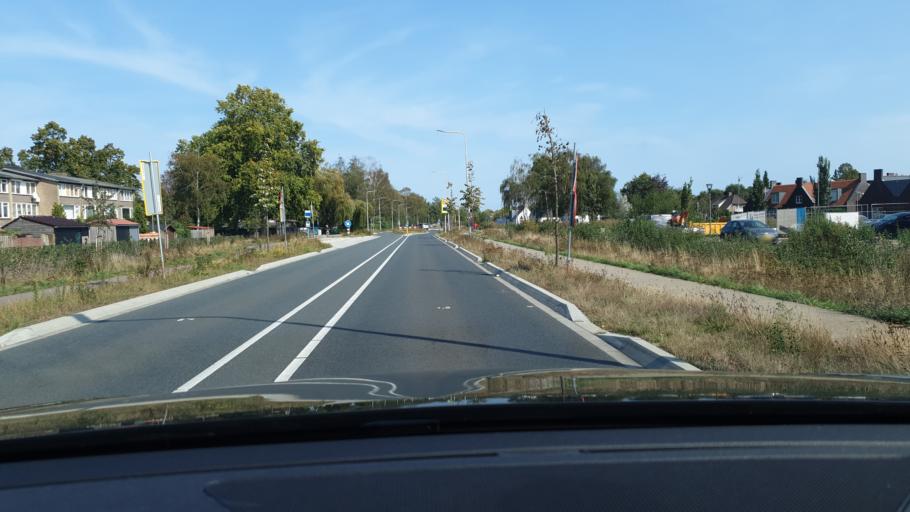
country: NL
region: North Brabant
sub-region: Gemeente Laarbeek
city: Aarle-Rixtel
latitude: 51.5262
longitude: 5.6337
